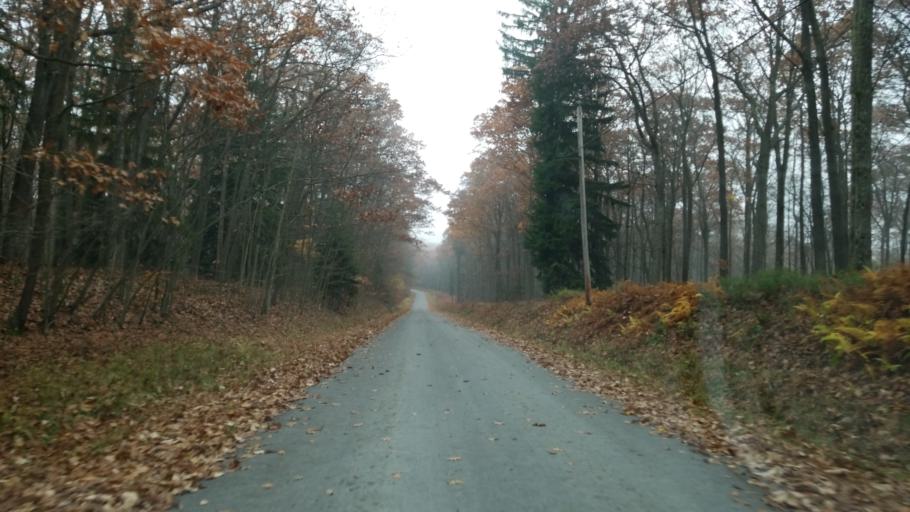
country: US
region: Pennsylvania
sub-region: Clearfield County
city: Clearfield
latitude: 41.1055
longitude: -78.5260
